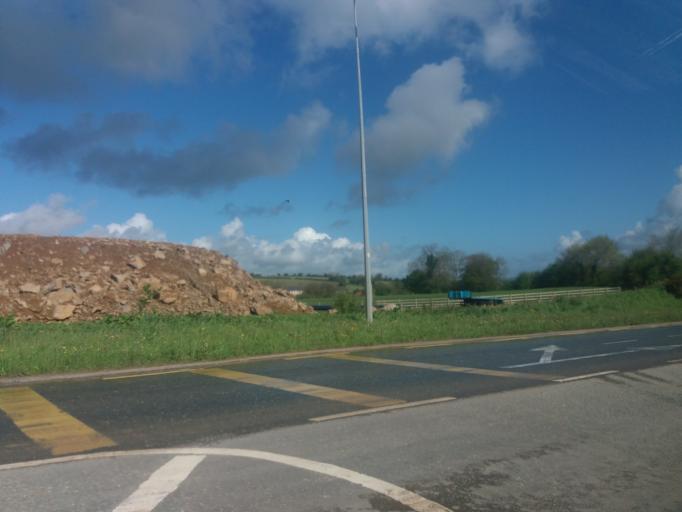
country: IE
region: Leinster
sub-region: Loch Garman
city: Enniscorthy
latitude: 52.5427
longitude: -6.5509
